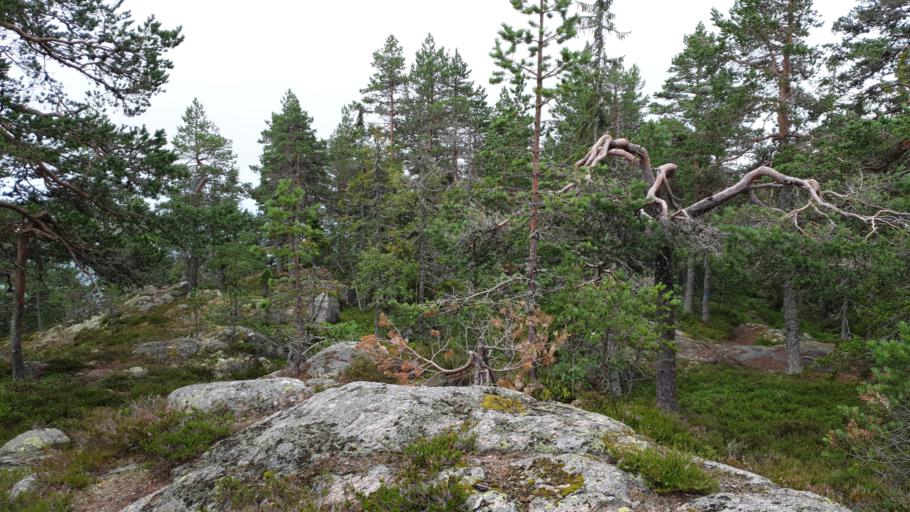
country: SE
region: Gaevleborg
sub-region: Hudiksvalls Kommun
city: Sorforsa
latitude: 61.6441
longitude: 16.7652
